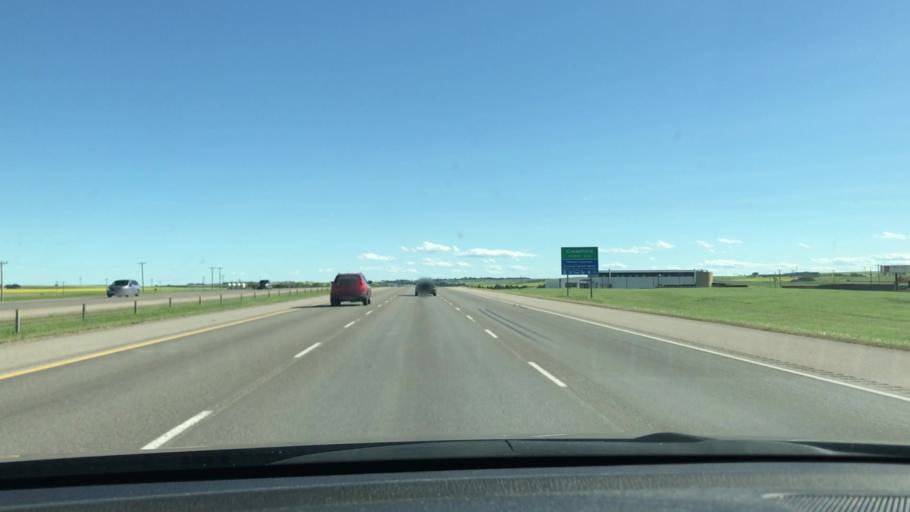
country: CA
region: Alberta
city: Crossfield
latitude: 51.4969
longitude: -114.0254
